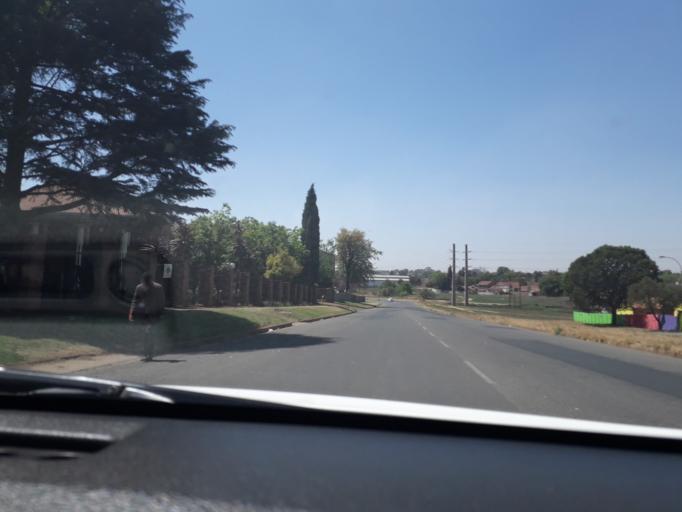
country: ZA
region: Gauteng
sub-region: City of Johannesburg Metropolitan Municipality
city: Modderfontein
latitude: -26.1205
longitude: 28.2206
